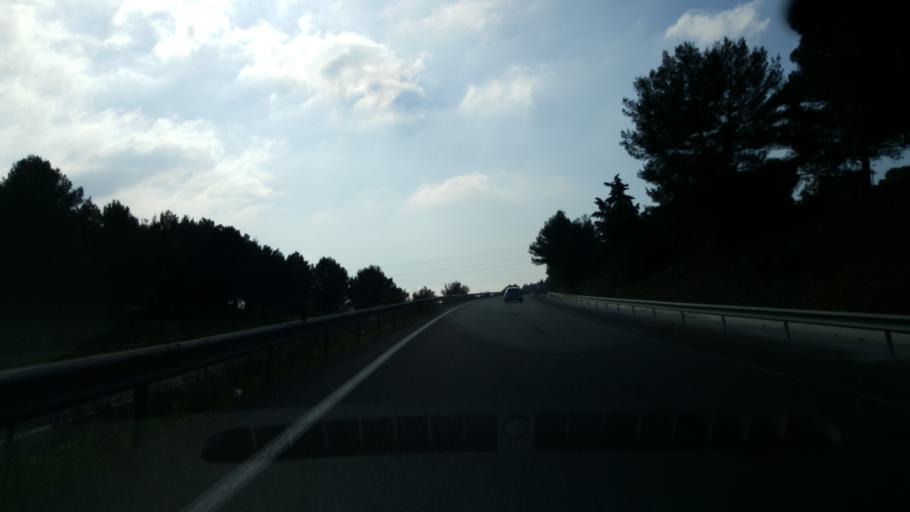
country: FR
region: Provence-Alpes-Cote d'Azur
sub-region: Departement des Bouches-du-Rhone
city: Auriol
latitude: 43.3554
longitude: 5.6246
